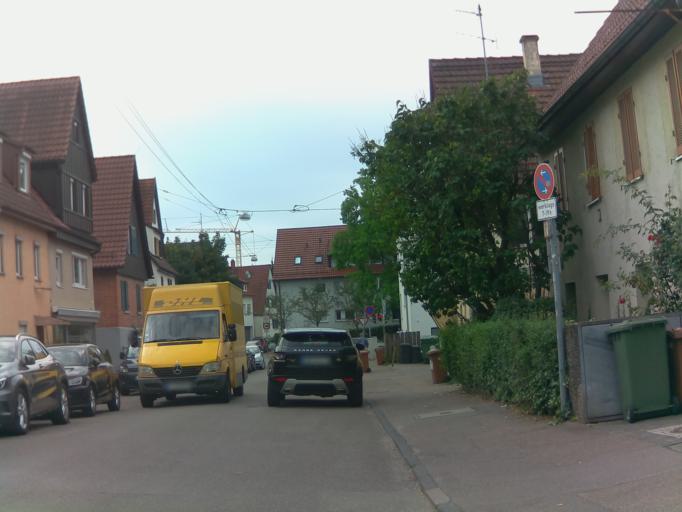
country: DE
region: Baden-Wuerttemberg
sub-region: Regierungsbezirk Stuttgart
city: Leinfelden-Echterdingen
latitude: 48.7285
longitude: 9.1442
